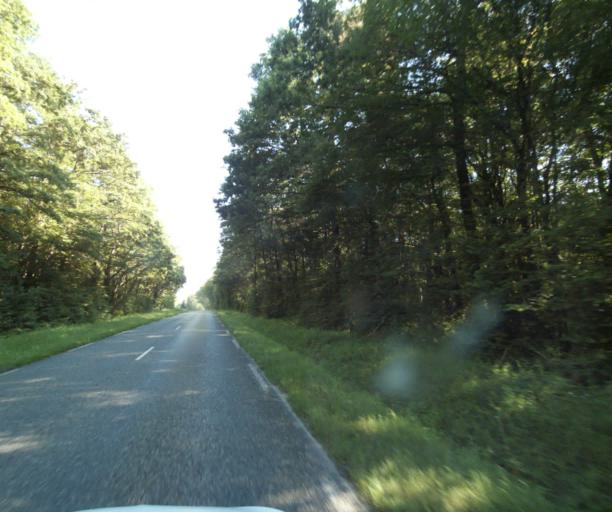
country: FR
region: Rhone-Alpes
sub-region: Departement de la Haute-Savoie
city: Messery
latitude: 46.3384
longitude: 6.2917
